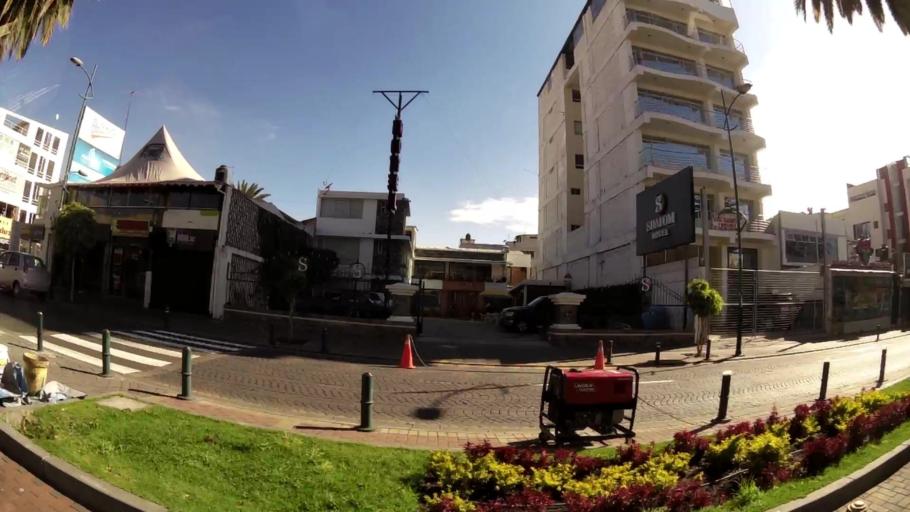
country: EC
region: Chimborazo
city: Riobamba
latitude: -1.6674
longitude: -78.6563
